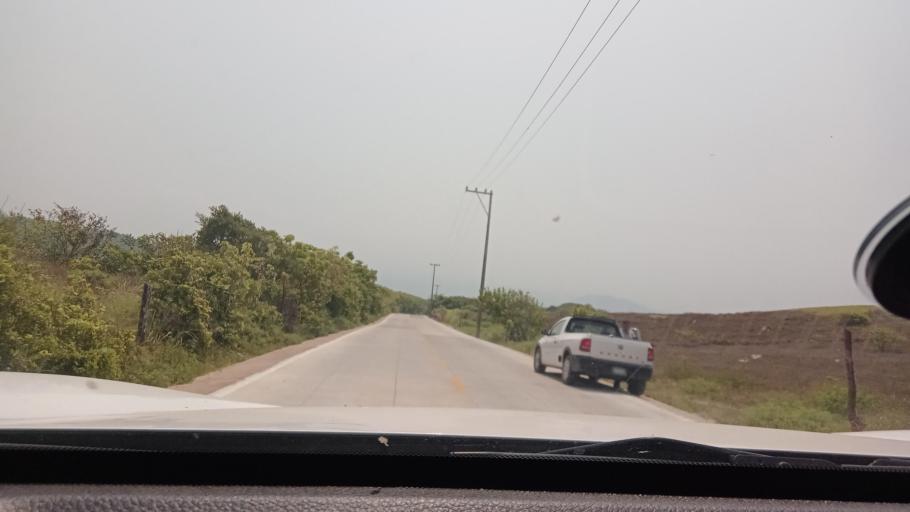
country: MX
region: Veracruz
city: Catemaco
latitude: 18.5561
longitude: -94.9975
